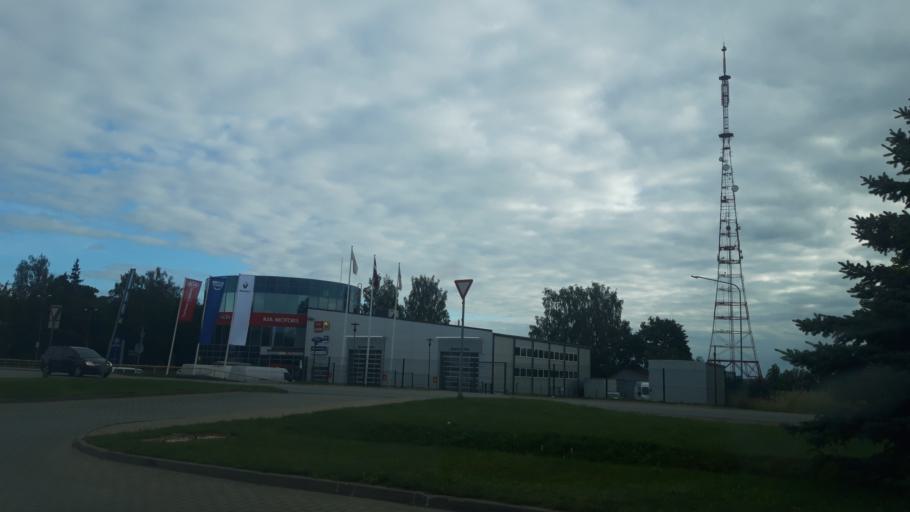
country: LV
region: Koceni
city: Koceni
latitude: 57.5242
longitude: 25.3793
